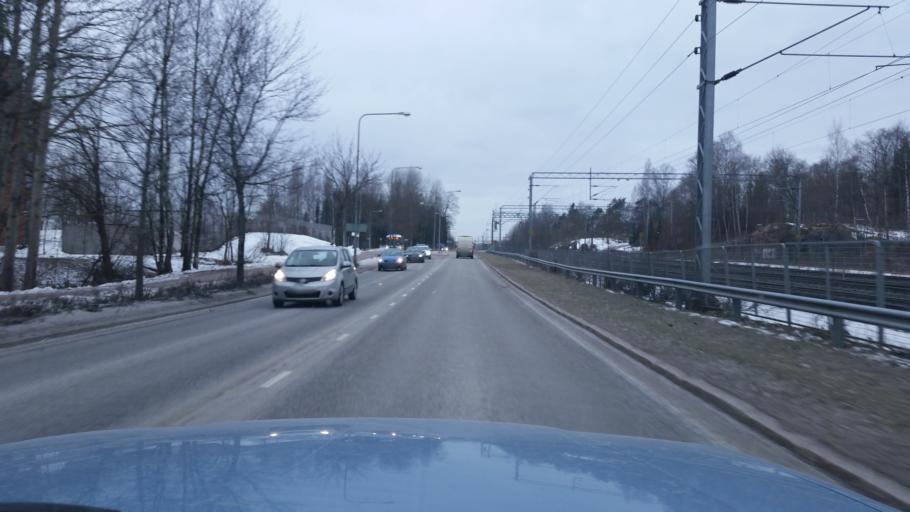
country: FI
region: Uusimaa
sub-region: Helsinki
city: Vantaa
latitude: 60.2477
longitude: 25.0047
